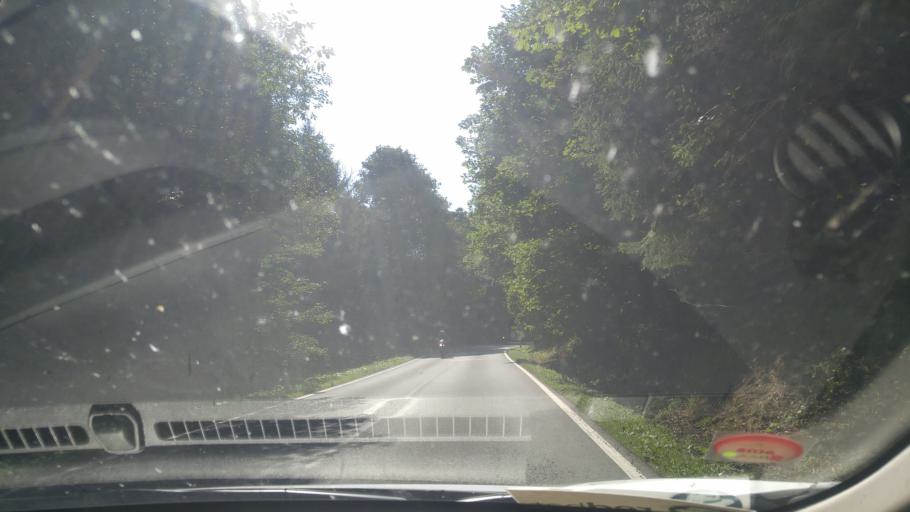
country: CZ
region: Olomoucky
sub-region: Okres Sumperk
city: Stare Mesto
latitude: 50.1645
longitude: 17.0268
